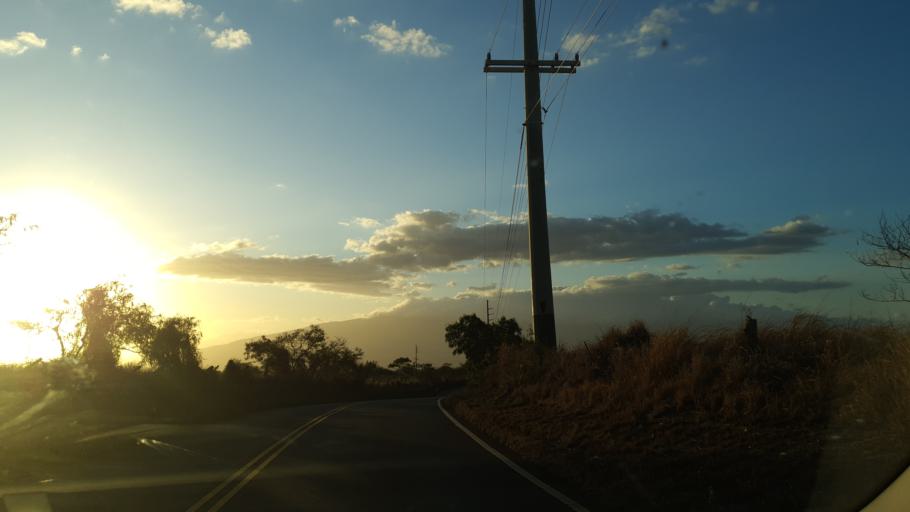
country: US
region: Hawaii
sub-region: Maui County
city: Pukalani
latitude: 20.7905
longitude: -156.3557
